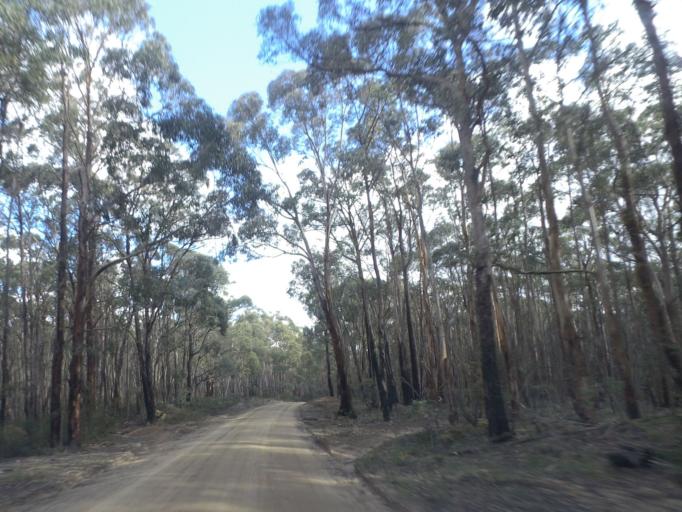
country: AU
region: Victoria
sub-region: Moorabool
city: Bacchus Marsh
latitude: -37.4488
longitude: 144.4826
